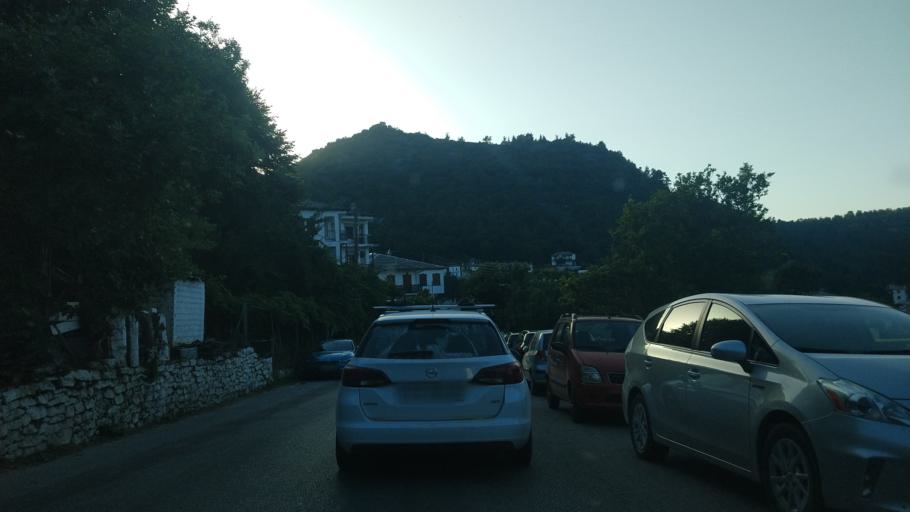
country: GR
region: East Macedonia and Thrace
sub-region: Nomos Kavalas
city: Potamia
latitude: 40.7297
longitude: 24.7310
